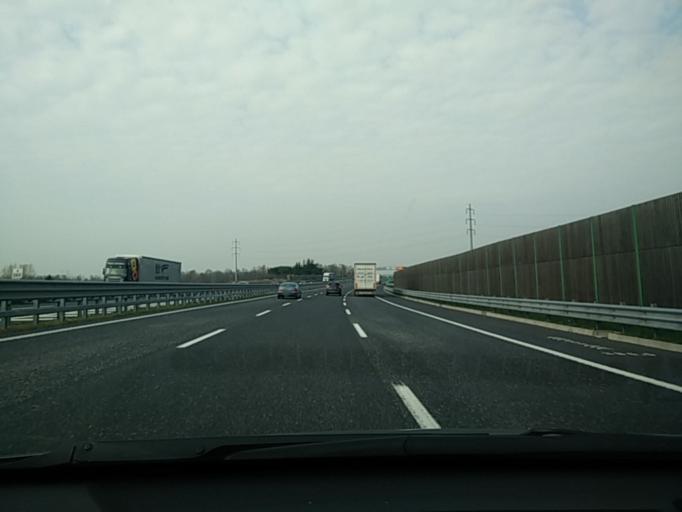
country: IT
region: Veneto
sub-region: Provincia di Venezia
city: Maerne
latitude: 45.5245
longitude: 12.1398
